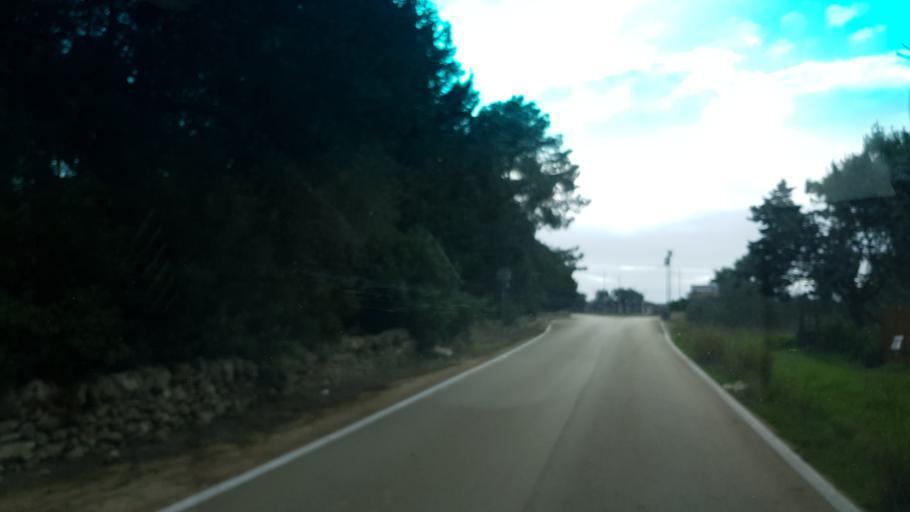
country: IT
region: Apulia
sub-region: Provincia di Brindisi
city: San Vito dei Normanni
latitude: 40.6965
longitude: 17.7592
